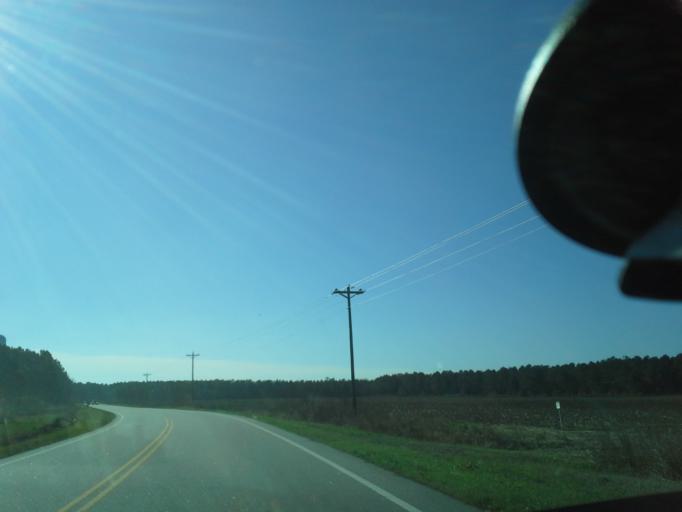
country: US
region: North Carolina
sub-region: Beaufort County
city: Belhaven
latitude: 35.5779
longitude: -76.6851
